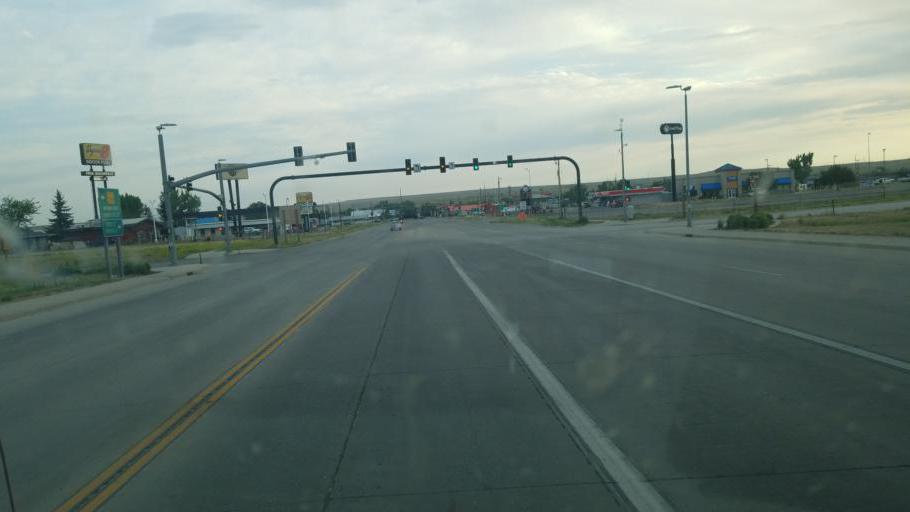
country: US
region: Wyoming
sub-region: Natrona County
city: Evansville
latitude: 42.8545
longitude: -106.2707
